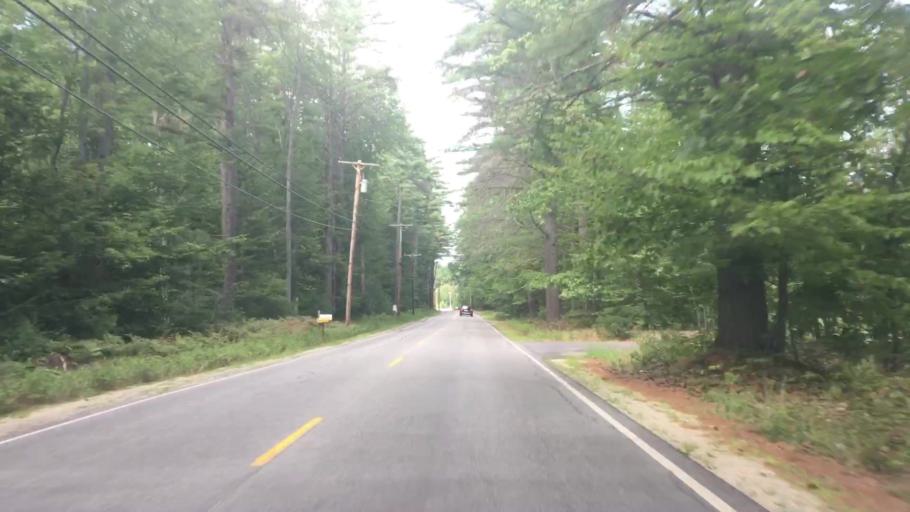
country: US
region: Maine
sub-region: Oxford County
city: Oxford
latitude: 44.1176
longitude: -70.5057
